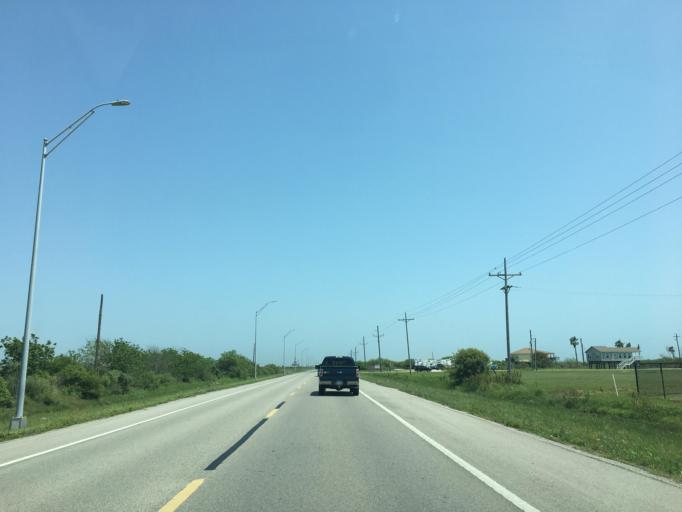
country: US
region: Texas
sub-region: Galveston County
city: Galveston
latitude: 29.3763
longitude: -94.7502
